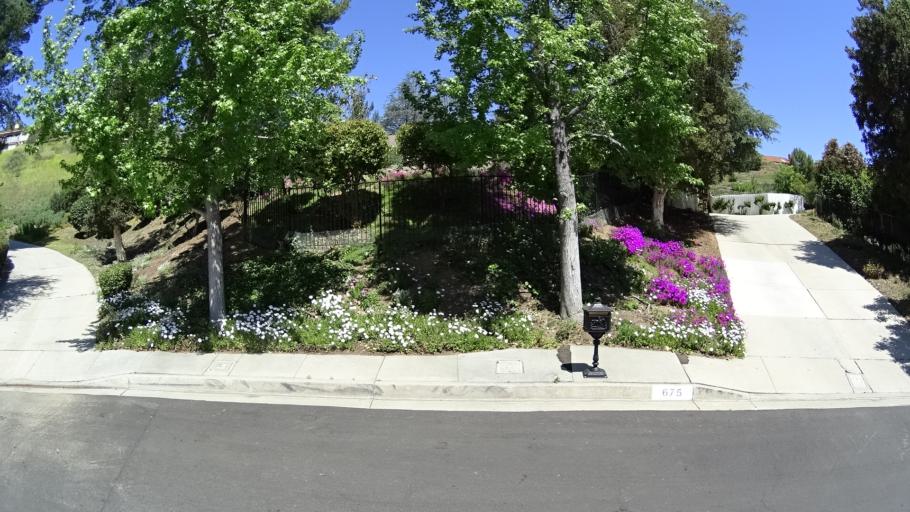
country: US
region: California
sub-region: Ventura County
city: Casa Conejo
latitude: 34.2013
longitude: -118.8933
